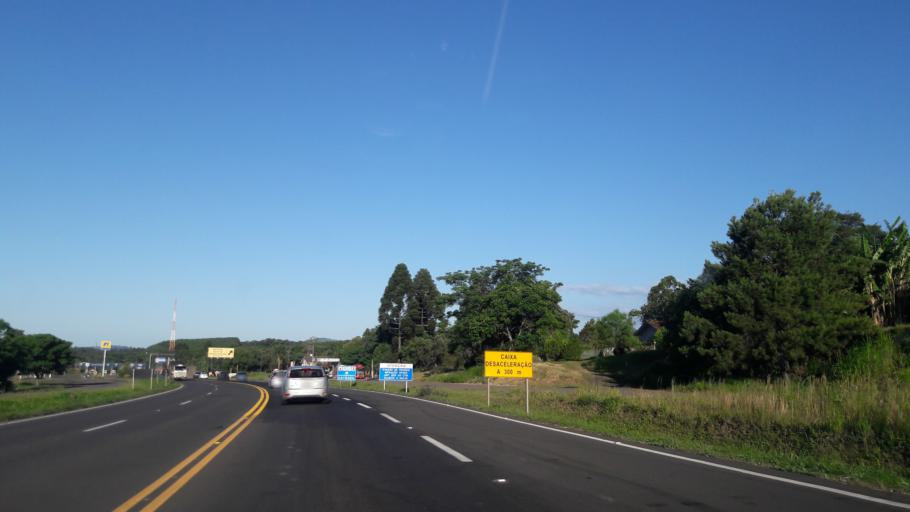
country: BR
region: Parana
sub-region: Prudentopolis
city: Prudentopolis
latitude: -25.3128
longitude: -51.1730
